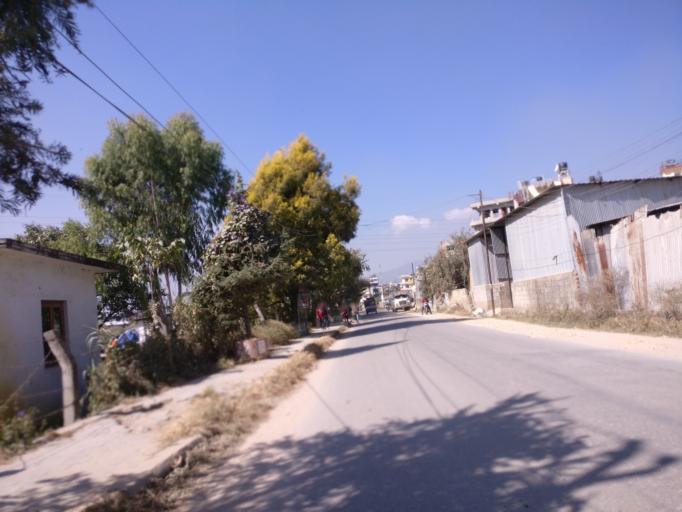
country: NP
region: Central Region
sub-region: Bagmati Zone
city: Patan
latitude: 27.6759
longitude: 85.3384
